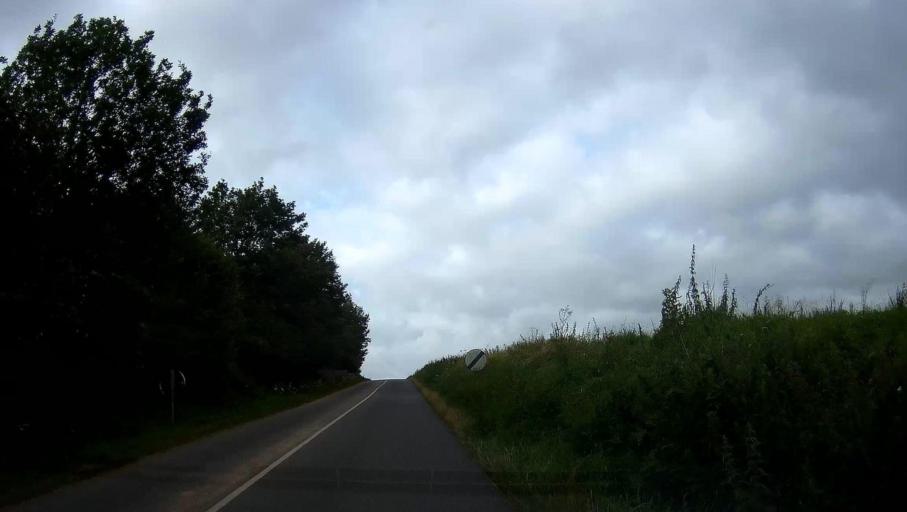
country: FR
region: Champagne-Ardenne
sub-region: Departement des Ardennes
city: Chateau-Porcien
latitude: 49.6236
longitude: 4.2351
